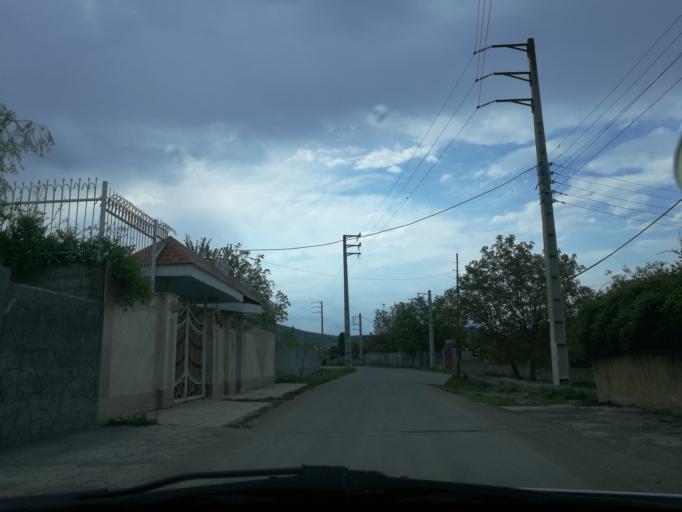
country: IR
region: Mazandaran
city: `Abbasabad
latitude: 36.5332
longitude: 51.2244
